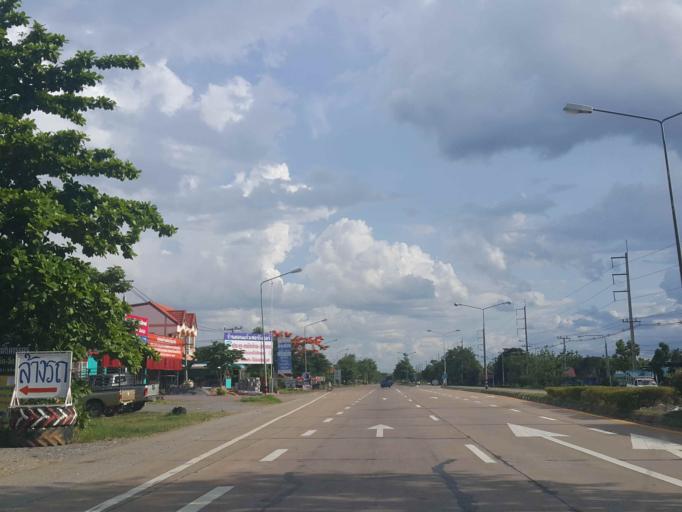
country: TH
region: Phrae
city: Sung Men
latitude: 18.0239
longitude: 100.1107
